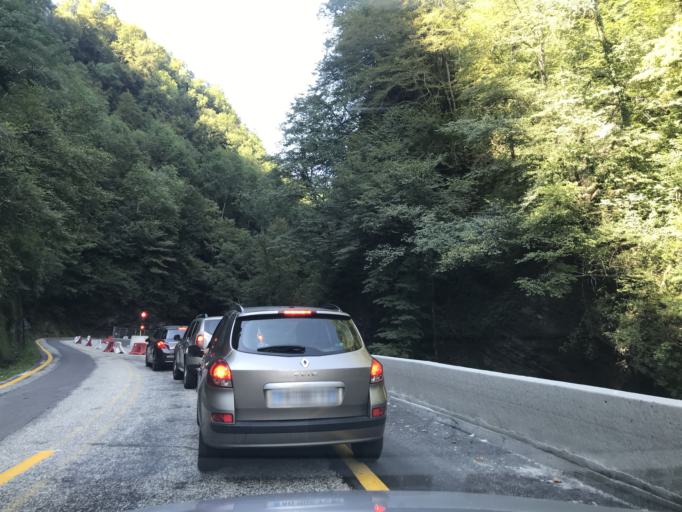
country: FR
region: Rhone-Alpes
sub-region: Departement de la Savoie
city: La Rochette
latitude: 45.4325
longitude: 6.0945
